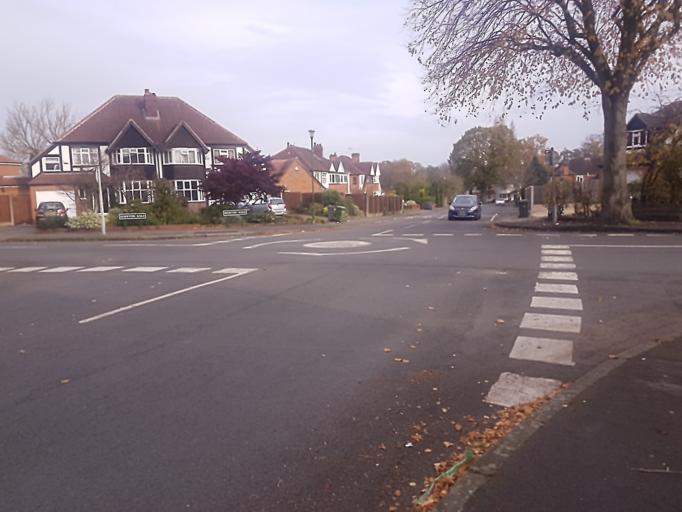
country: GB
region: England
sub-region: City and Borough of Birmingham
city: Acocks Green
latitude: 52.4340
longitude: -1.7973
